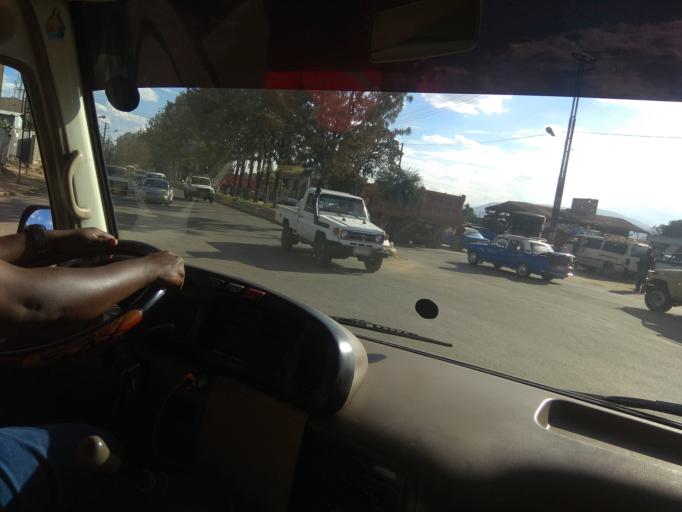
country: ET
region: Adis Abeba
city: Addis Ababa
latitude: 9.0210
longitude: 38.7477
